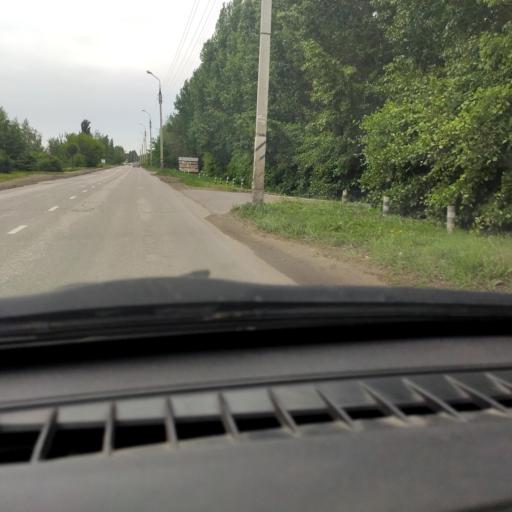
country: RU
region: Samara
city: Tol'yatti
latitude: 53.5608
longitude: 49.3949
